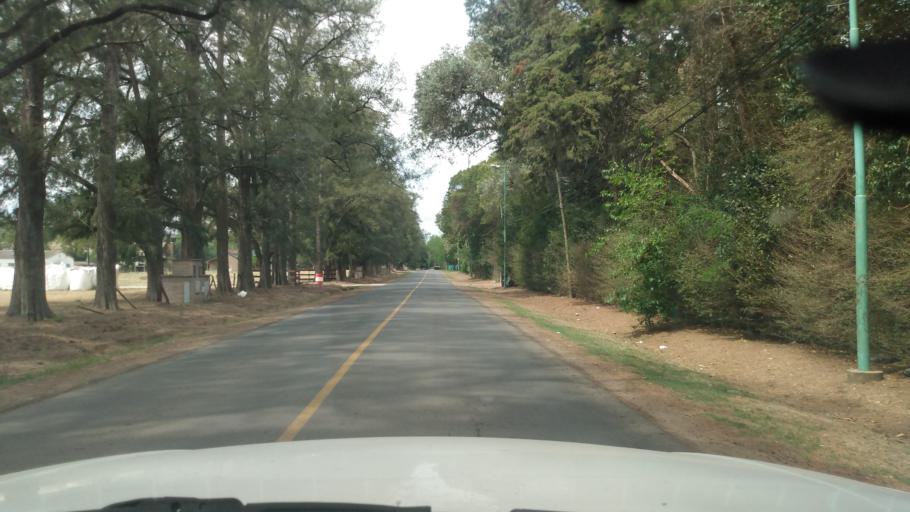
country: AR
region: Buenos Aires
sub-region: Partido de Lujan
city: Lujan
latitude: -34.5547
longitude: -59.1989
